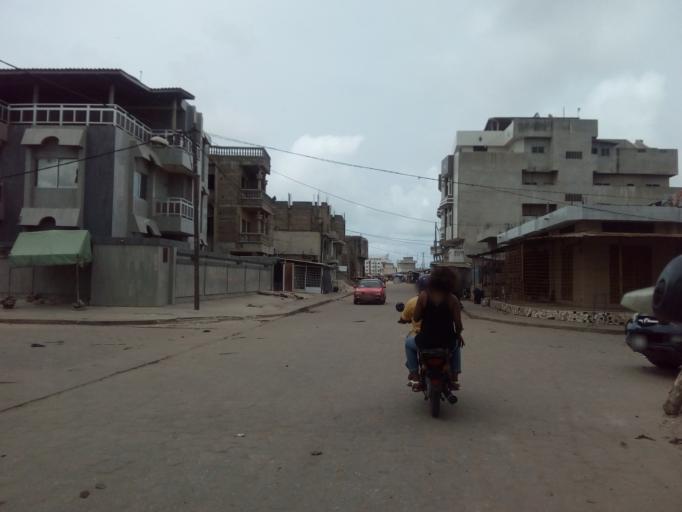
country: BJ
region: Littoral
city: Cotonou
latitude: 6.3765
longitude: 2.4393
